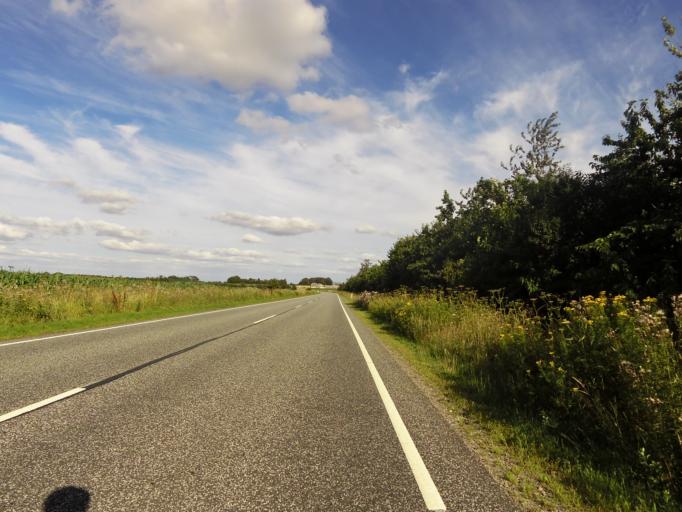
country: DK
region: South Denmark
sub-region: Haderslev Kommune
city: Gram
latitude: 55.2307
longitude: 8.9695
